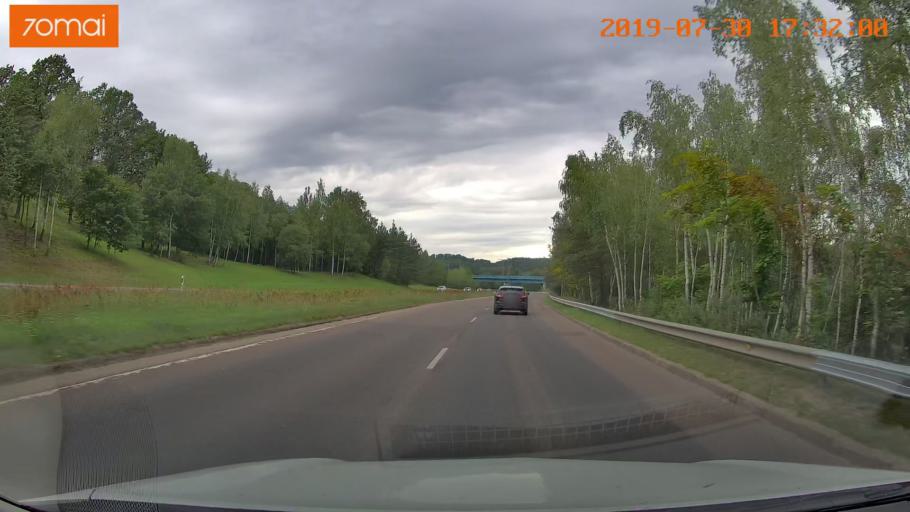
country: LT
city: Skaidiskes
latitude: 54.6913
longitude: 25.3939
